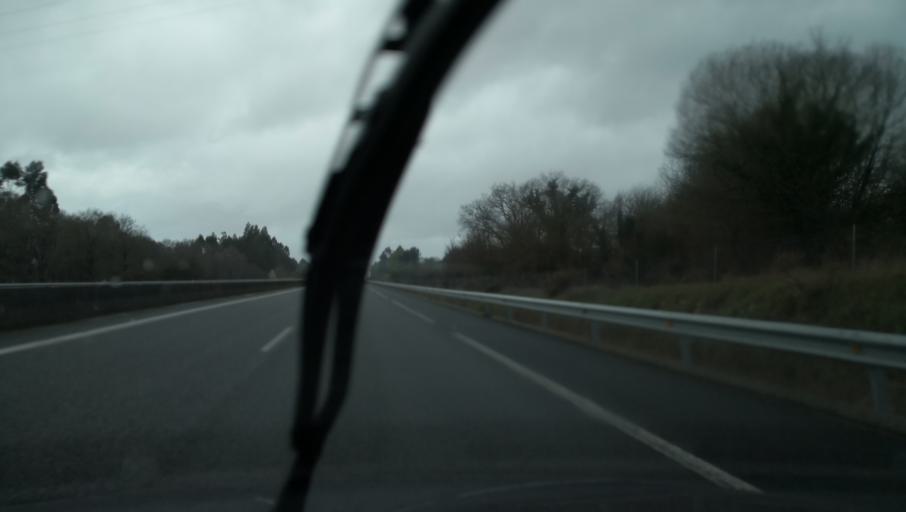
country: ES
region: Galicia
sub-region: Provincia de Pontevedra
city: Silleda
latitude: 42.6906
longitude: -8.1825
